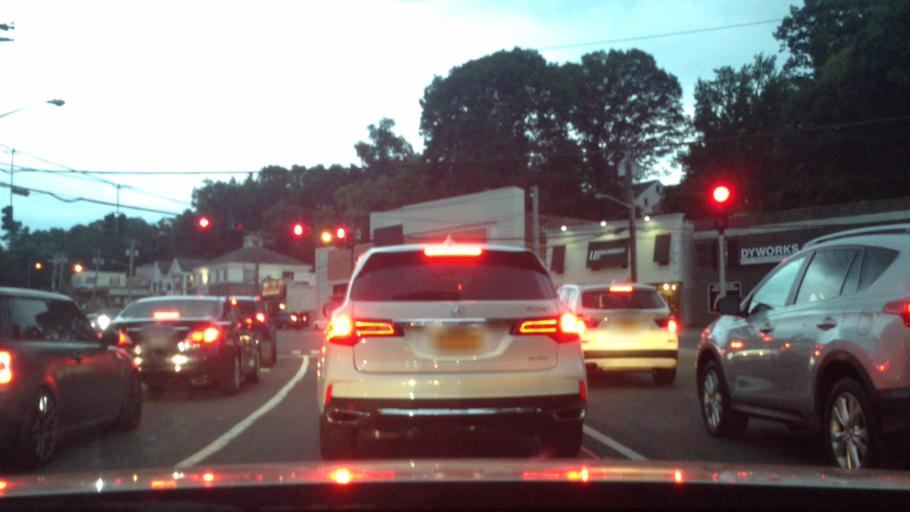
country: US
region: New York
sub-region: Nassau County
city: Thomaston
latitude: 40.7882
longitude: -73.7060
